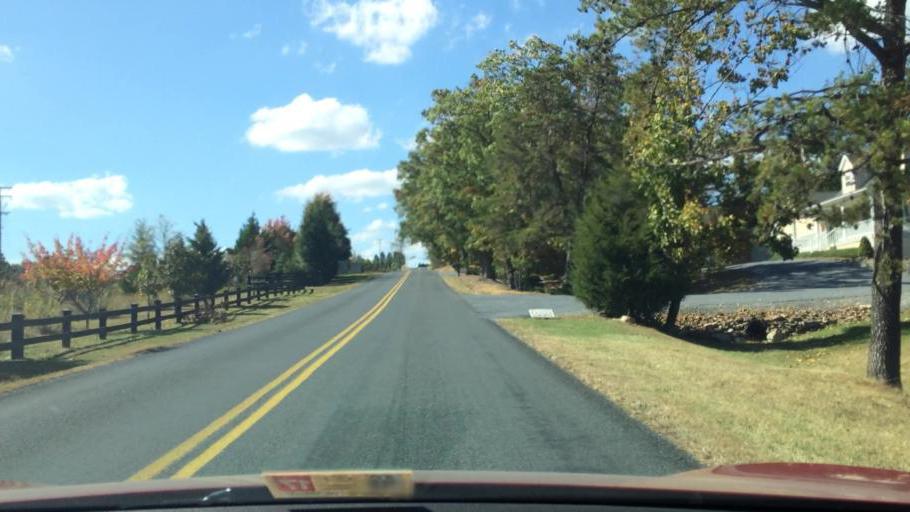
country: US
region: Virginia
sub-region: Frederick County
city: Shawnee Land
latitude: 39.3245
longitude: -78.3122
